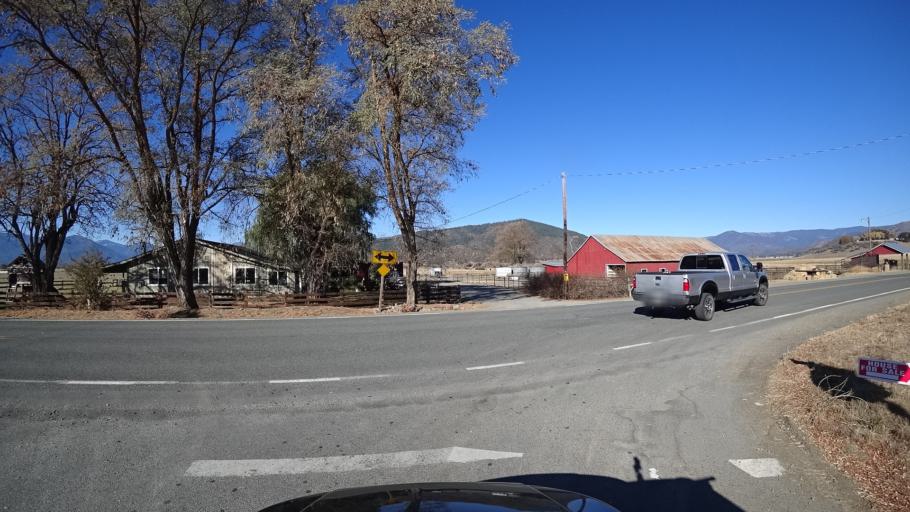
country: US
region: California
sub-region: Siskiyou County
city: Yreka
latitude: 41.5791
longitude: -122.8366
